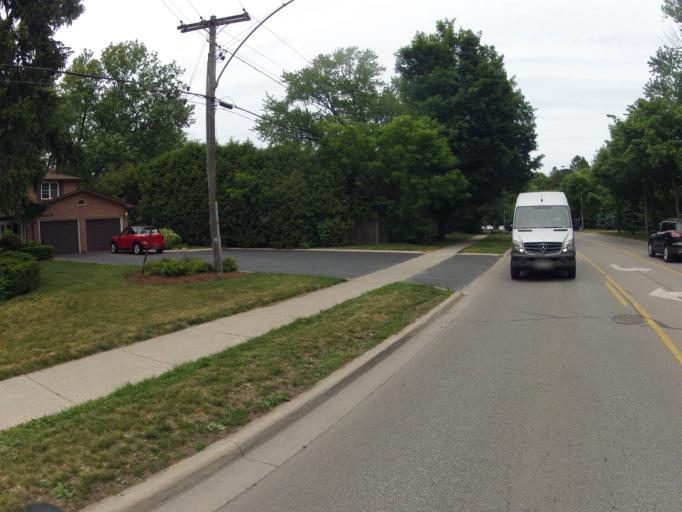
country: CA
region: Ontario
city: Burlington
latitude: 43.3484
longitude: -79.7588
